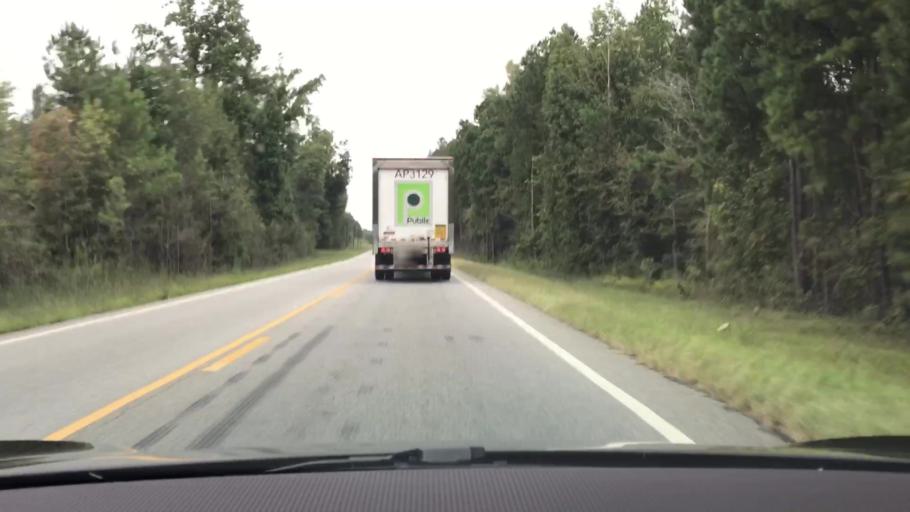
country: US
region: Georgia
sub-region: Greene County
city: Greensboro
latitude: 33.7014
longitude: -83.2828
